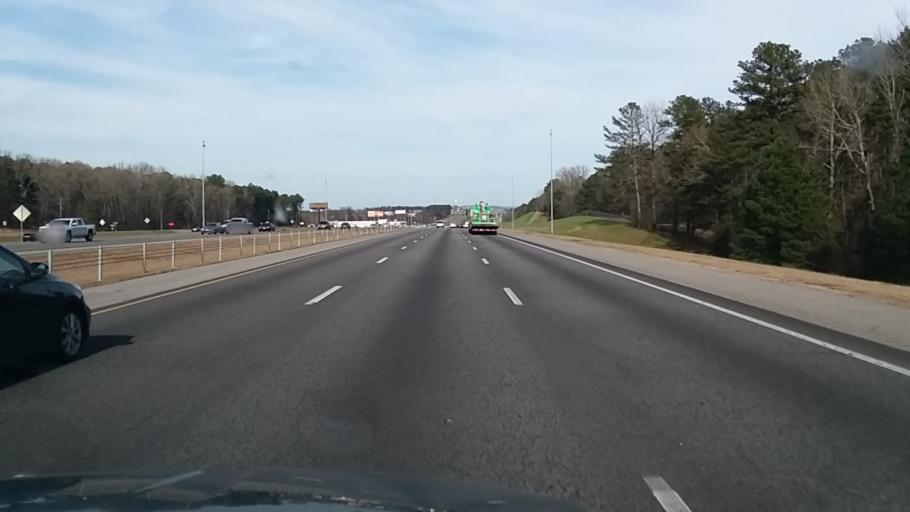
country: US
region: Alabama
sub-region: Madison County
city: Madison
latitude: 34.6911
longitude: -86.7132
